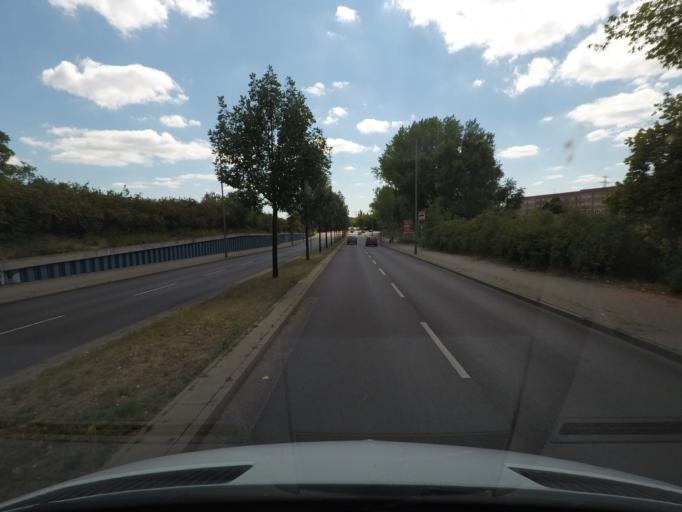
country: DE
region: Berlin
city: Biesdorf
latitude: 52.5127
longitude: 13.5444
